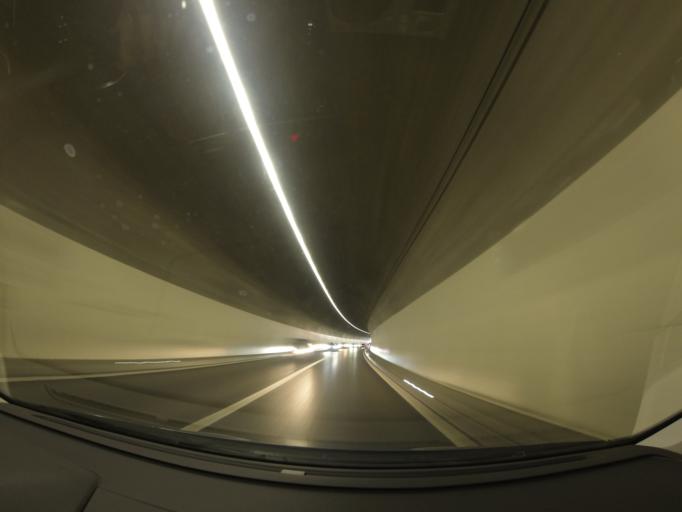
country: CH
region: Zurich
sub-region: Bezirk Hinwil
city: Rueti / Dorfzentrum, Suedl. Teil
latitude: 47.2414
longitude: 8.8621
